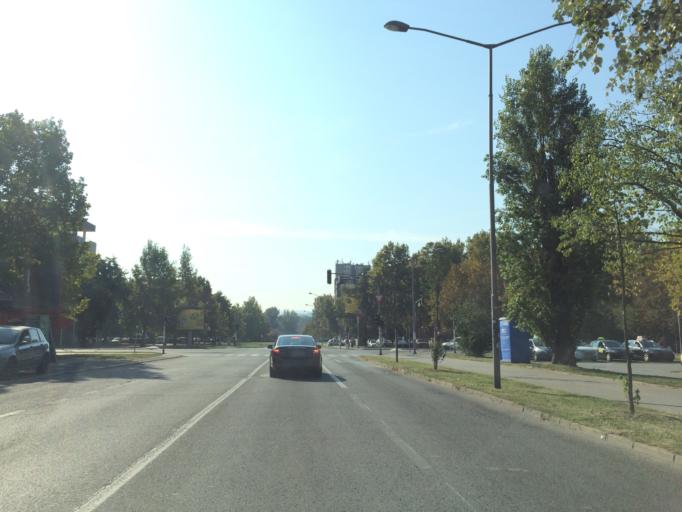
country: RS
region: Autonomna Pokrajina Vojvodina
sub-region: Juznobacki Okrug
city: Novi Sad
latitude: 45.2393
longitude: 19.8321
